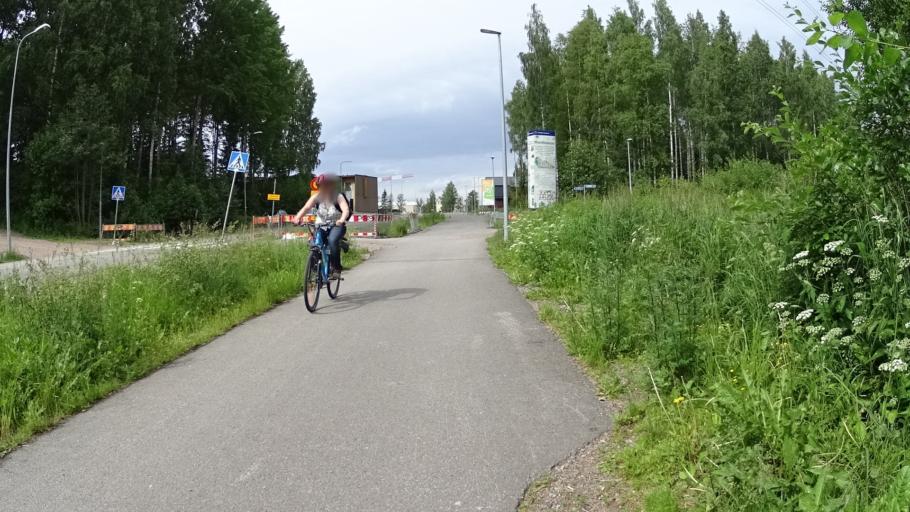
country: FI
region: Uusimaa
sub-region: Helsinki
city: Teekkarikylae
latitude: 60.2539
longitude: 24.8469
